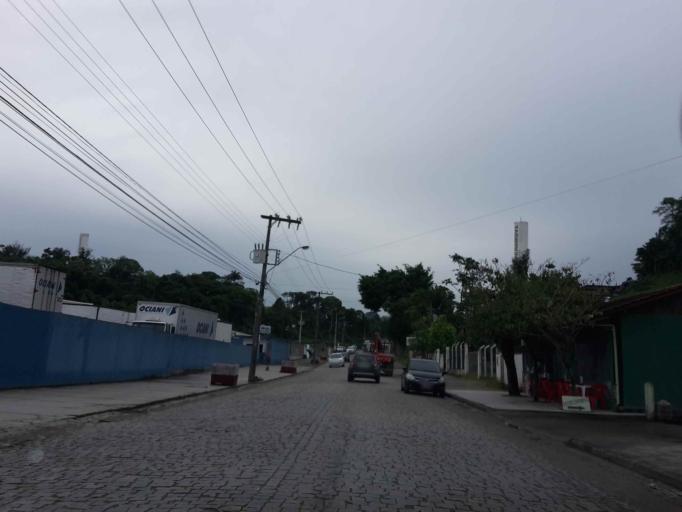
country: BR
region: Santa Catarina
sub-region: Blumenau
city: Blumenau
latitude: -26.8629
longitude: -49.0996
